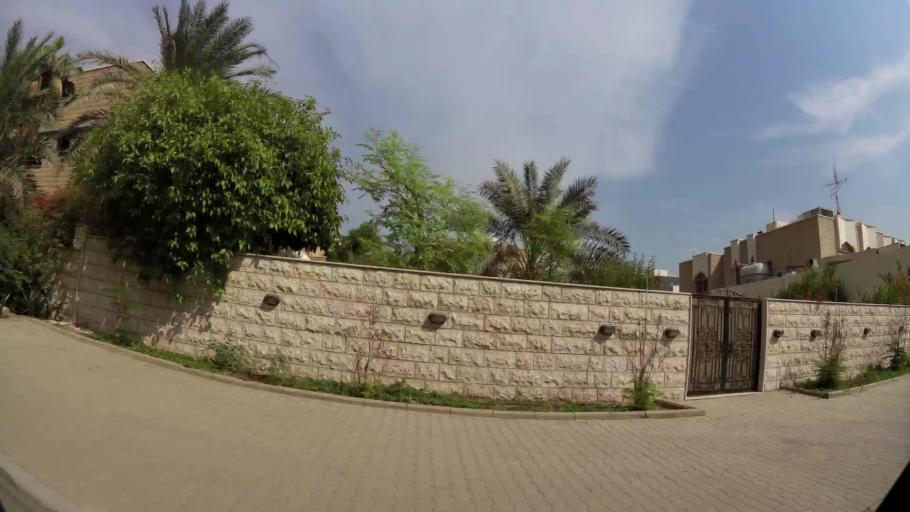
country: KW
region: Al Asimah
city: Ad Dasmah
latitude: 29.3544
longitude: 47.9889
